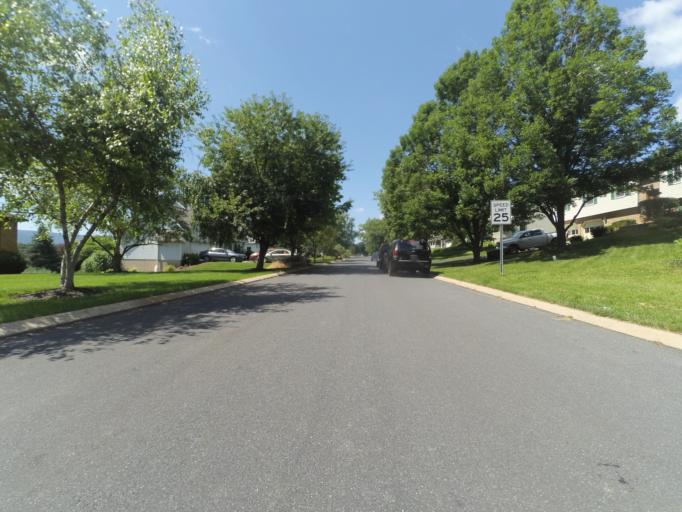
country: US
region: Pennsylvania
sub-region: Centre County
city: Lemont
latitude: 40.8044
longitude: -77.8310
